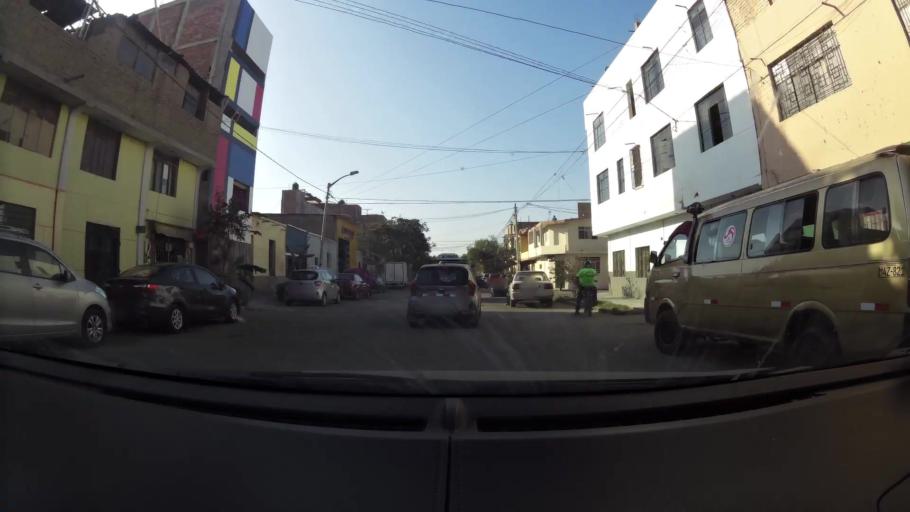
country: PE
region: Lambayeque
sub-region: Provincia de Chiclayo
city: Chiclayo
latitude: -6.7693
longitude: -79.8456
